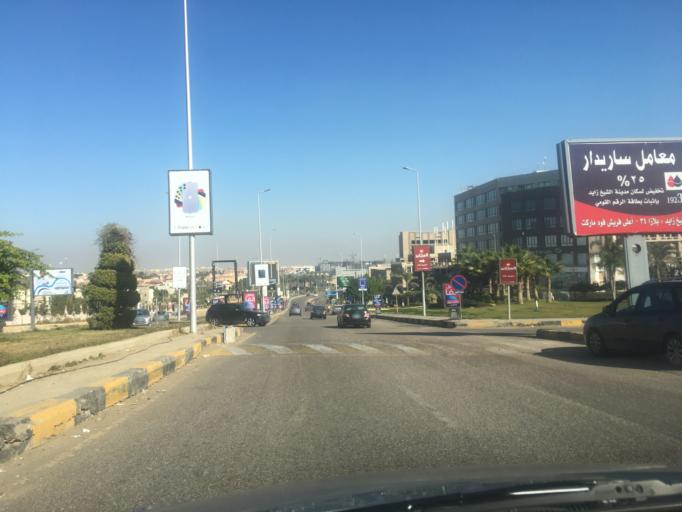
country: EG
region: Al Jizah
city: Awsim
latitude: 30.0198
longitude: 31.0010
